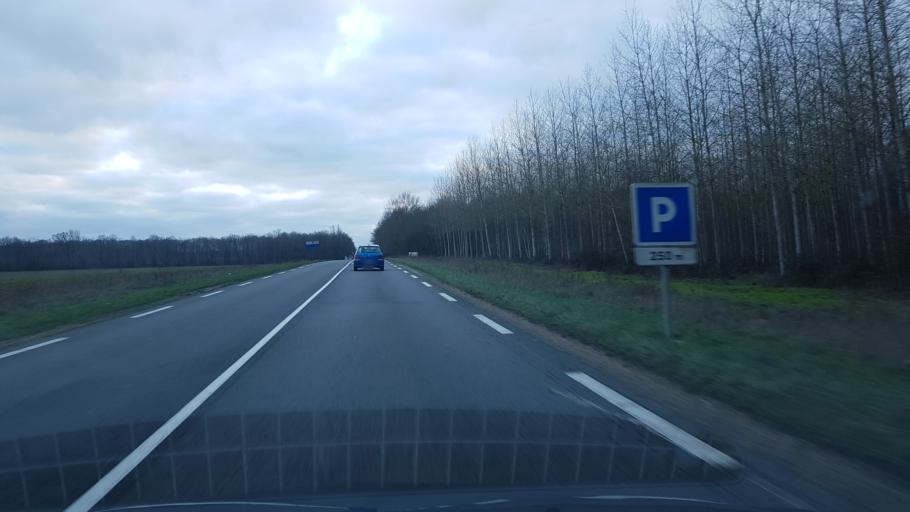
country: FR
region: Ile-de-France
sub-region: Departement de Seine-et-Marne
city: Villiers-Saint-Georges
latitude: 48.7096
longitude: 3.4719
